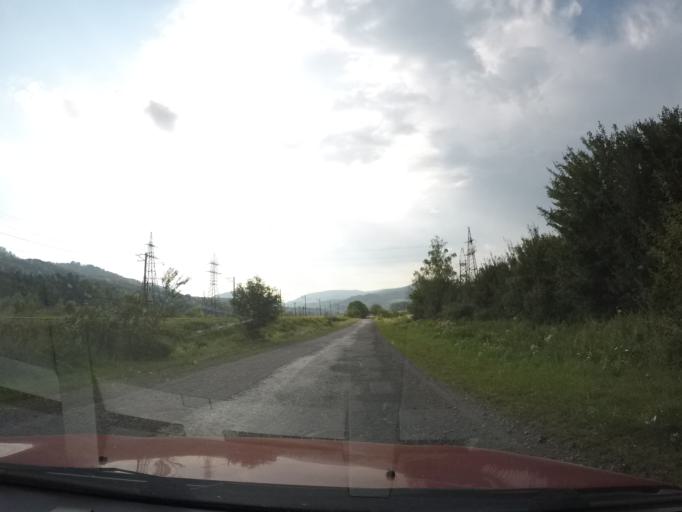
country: UA
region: Zakarpattia
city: Velykyi Bereznyi
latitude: 48.9422
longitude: 22.5756
